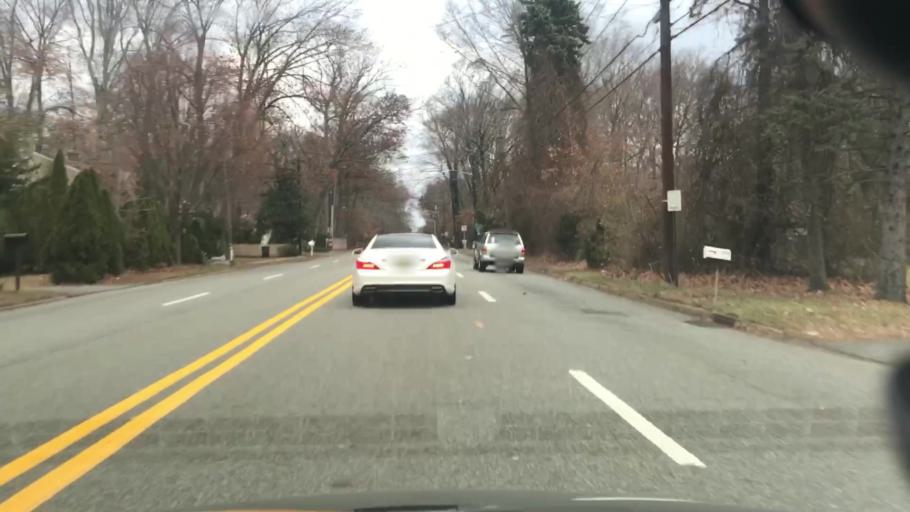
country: US
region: New Jersey
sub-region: Bergen County
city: River Edge
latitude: 40.9280
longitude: -74.0513
